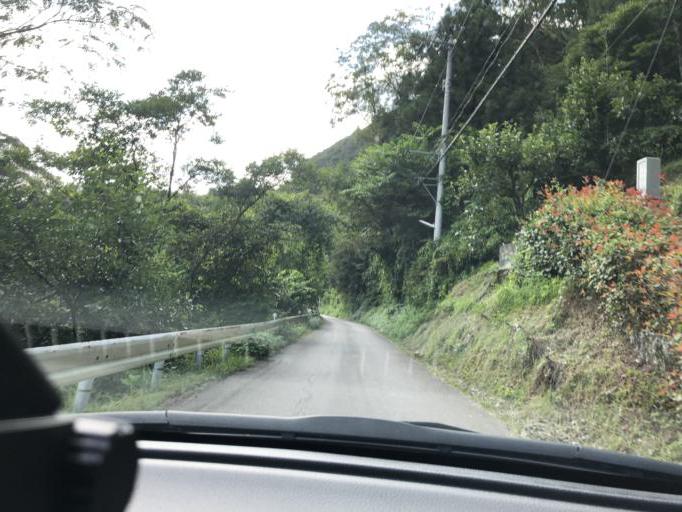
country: JP
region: Kochi
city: Kochi-shi
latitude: 33.6255
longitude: 133.5016
